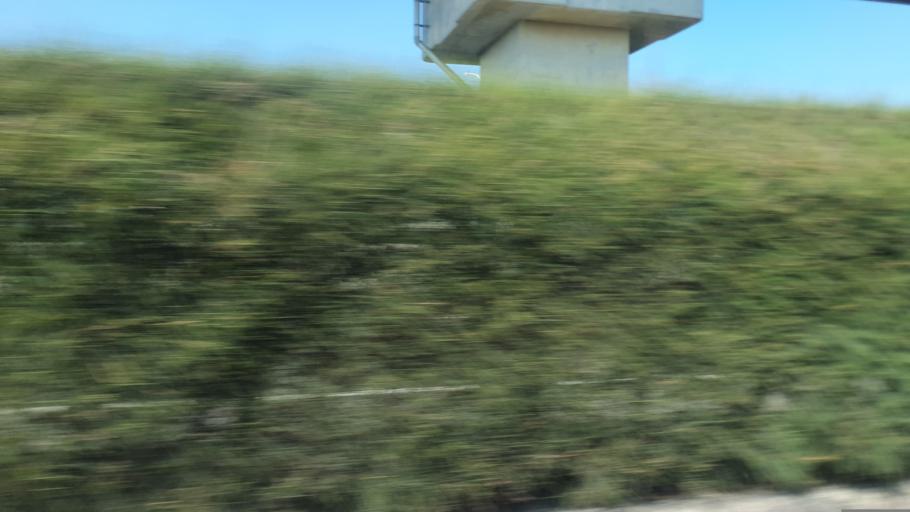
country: TW
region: Taiwan
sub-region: Tainan
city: Tainan
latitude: 23.0083
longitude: 120.2867
